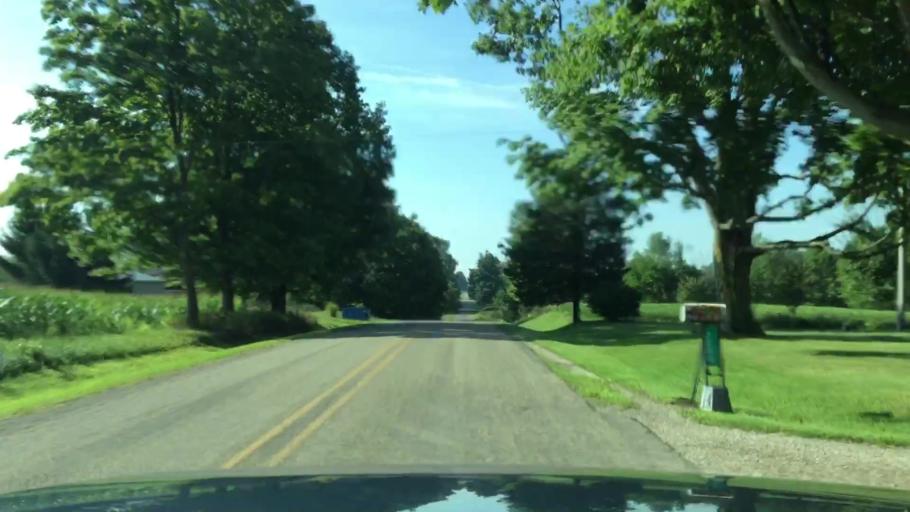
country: US
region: Michigan
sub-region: Lenawee County
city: Hudson
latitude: 41.8957
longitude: -84.4204
